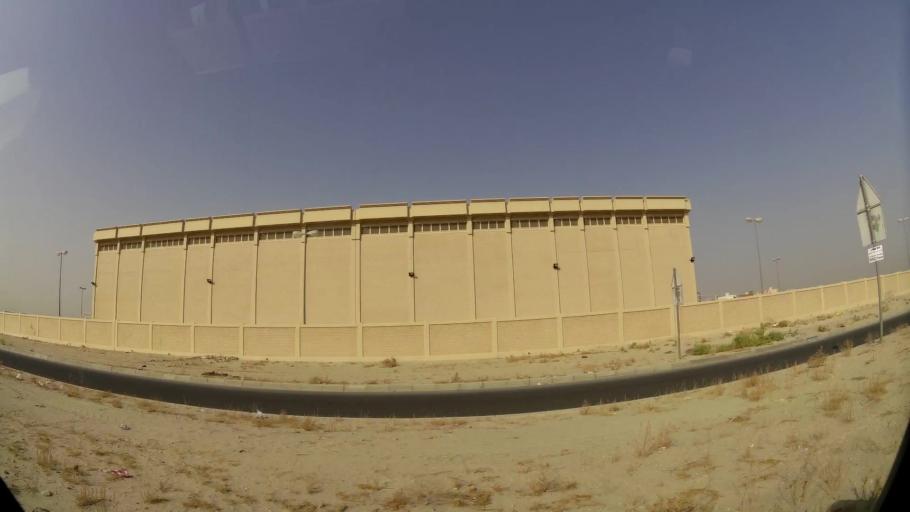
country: KW
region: Muhafazat al Jahra'
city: Al Jahra'
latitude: 29.3488
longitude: 47.7811
